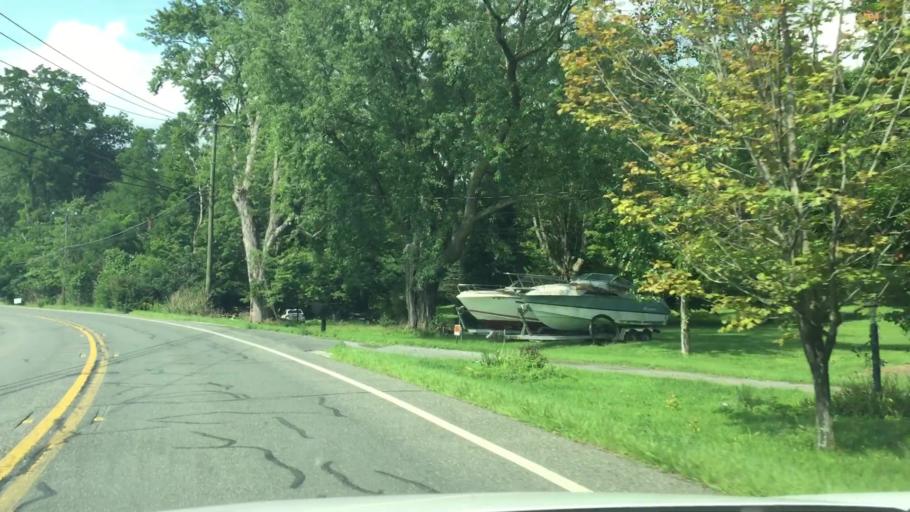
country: US
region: Massachusetts
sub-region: Berkshire County
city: Richmond
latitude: 42.4096
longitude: -73.3499
